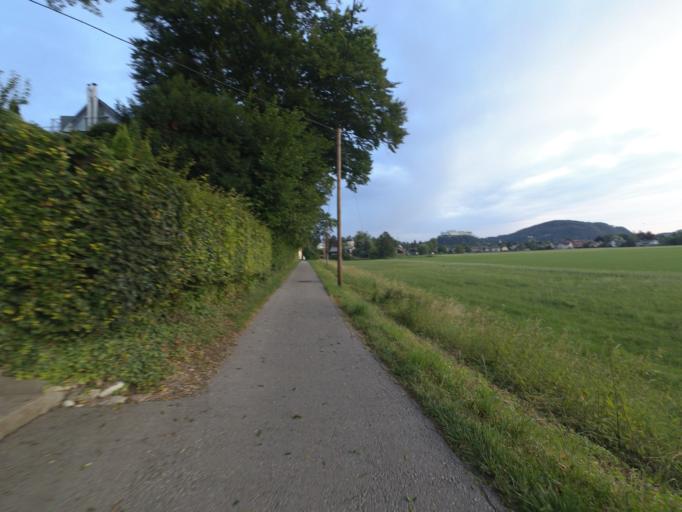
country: AT
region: Salzburg
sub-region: Salzburg Stadt
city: Salzburg
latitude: 47.7767
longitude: 13.0519
